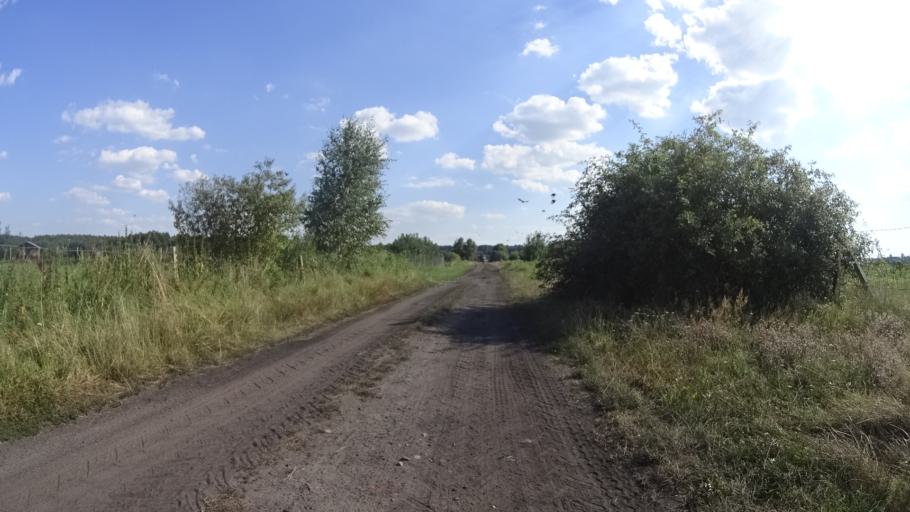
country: PL
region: Masovian Voivodeship
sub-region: Powiat bialobrzeski
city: Wysmierzyce
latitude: 51.6314
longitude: 20.8162
